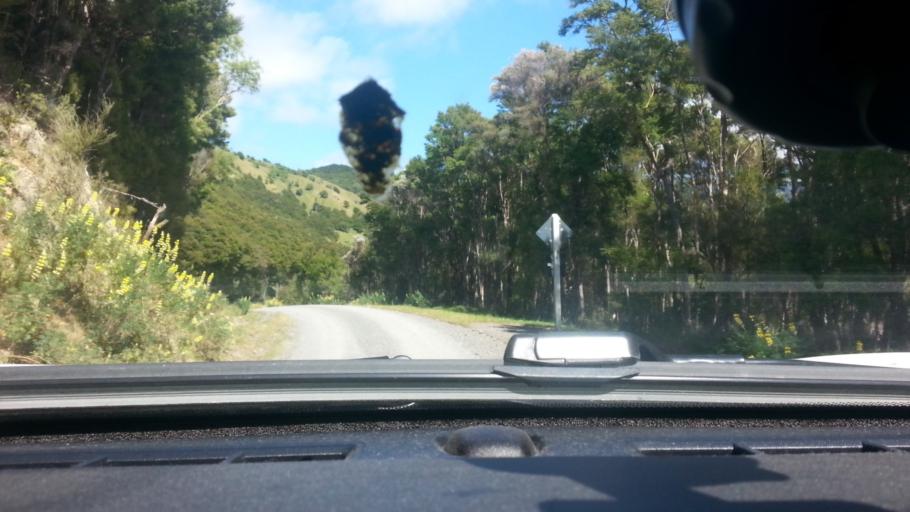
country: NZ
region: Wellington
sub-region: South Wairarapa District
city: Waipawa
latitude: -41.4647
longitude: 175.4296
